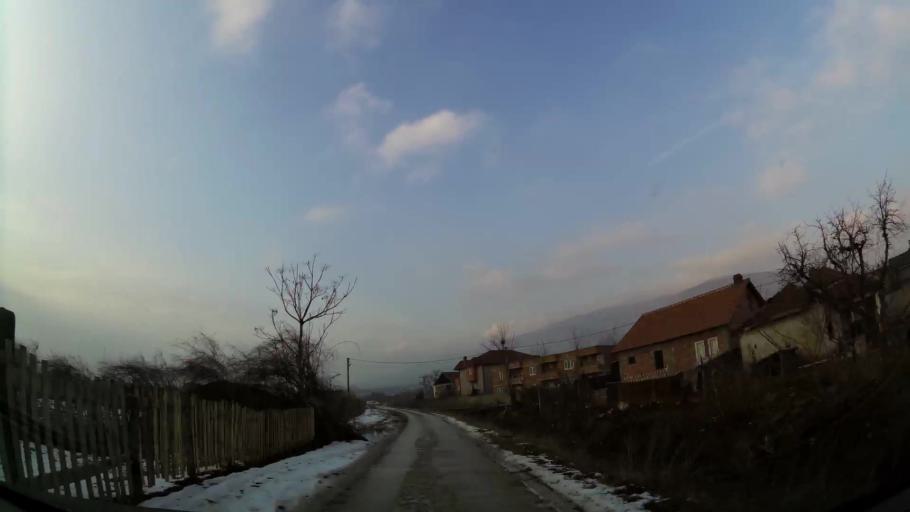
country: MK
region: Aracinovo
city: Arachinovo
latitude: 42.0225
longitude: 21.5589
